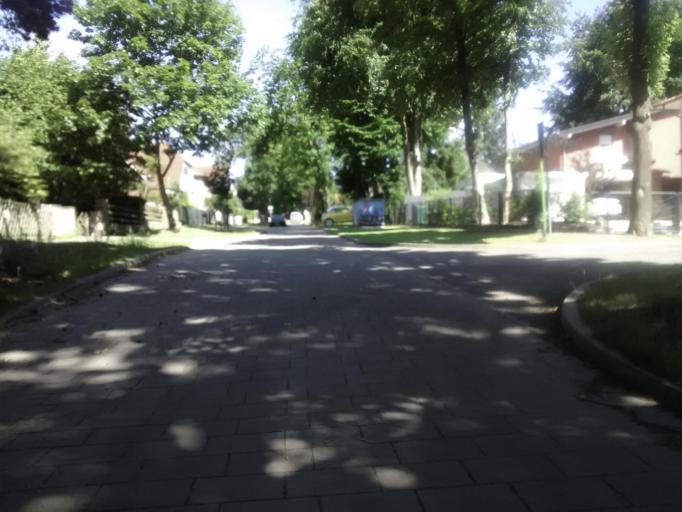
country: DE
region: Brandenburg
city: Birkenwerder
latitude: 52.6838
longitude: 13.2800
